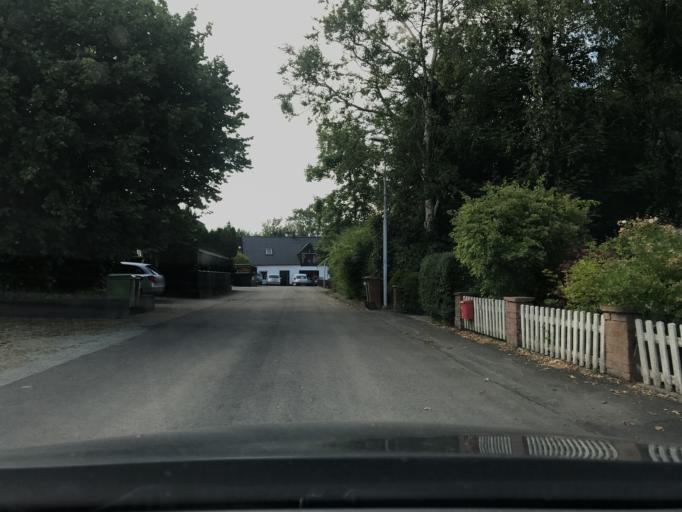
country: SE
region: Skane
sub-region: Simrishamns Kommun
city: Simrishamn
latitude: 55.5016
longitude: 14.1572
